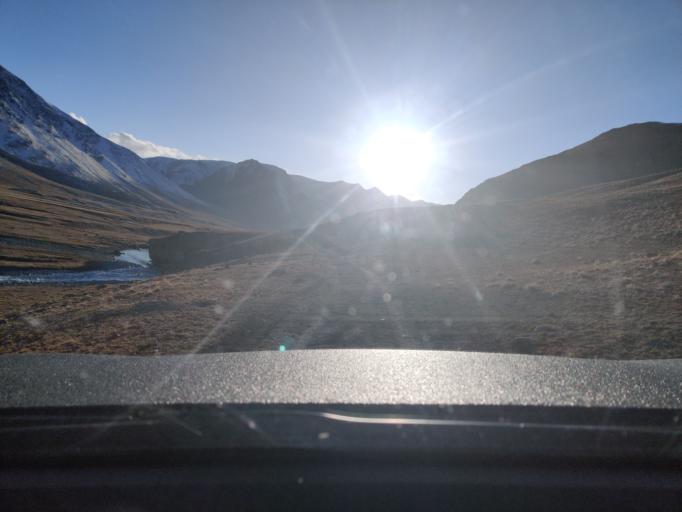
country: KG
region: Ysyk-Koel
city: Kadzhi-Say
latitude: 41.7592
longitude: 77.4313
